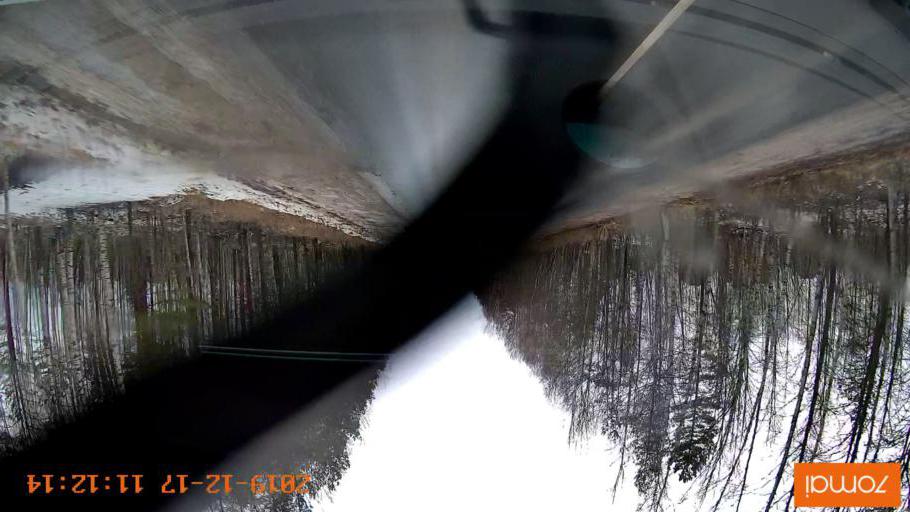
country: RU
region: Vladimir
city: Gus'-Khrustal'nyy
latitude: 55.5784
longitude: 40.6304
